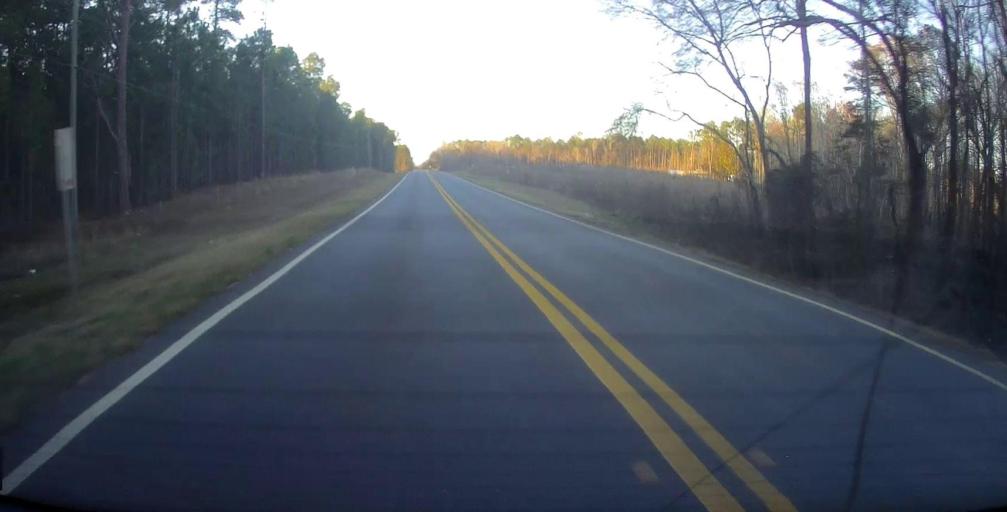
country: US
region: Georgia
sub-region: Dodge County
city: Chester
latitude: 32.3268
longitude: -83.0496
